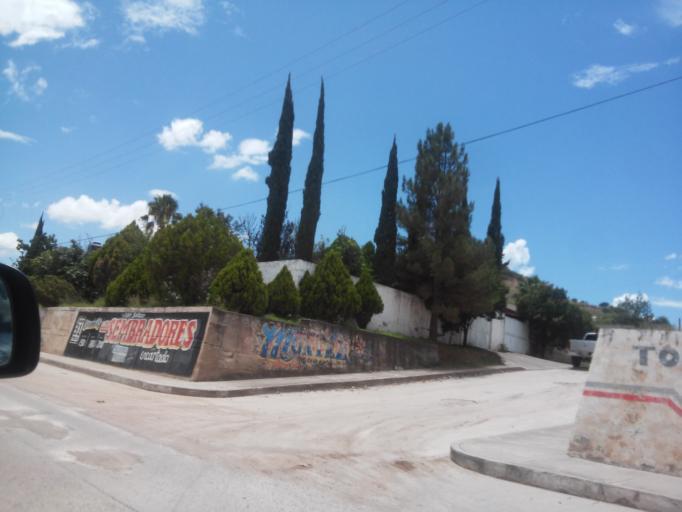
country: MX
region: Durango
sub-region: Santiago Papasquiaro
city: Santiago Papasquiaro
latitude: 25.0519
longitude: -105.4239
